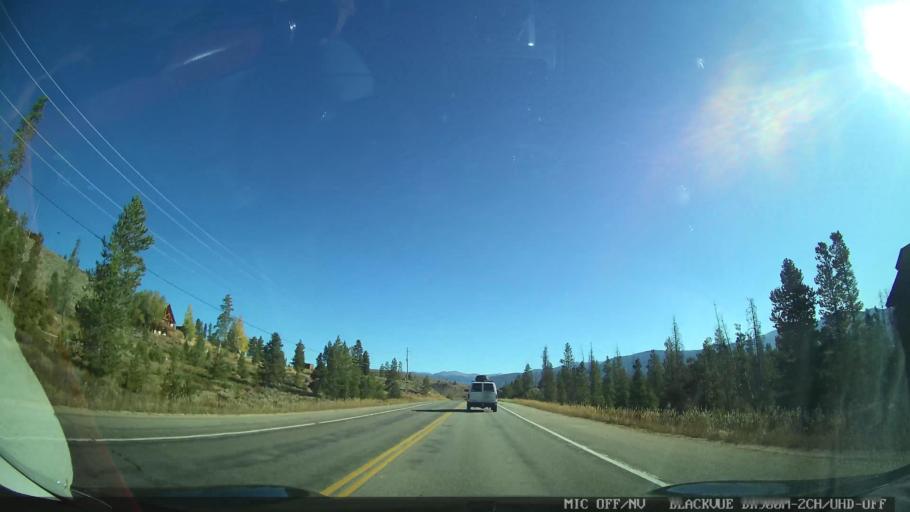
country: US
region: Colorado
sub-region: Grand County
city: Granby
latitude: 40.1763
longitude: -105.8985
